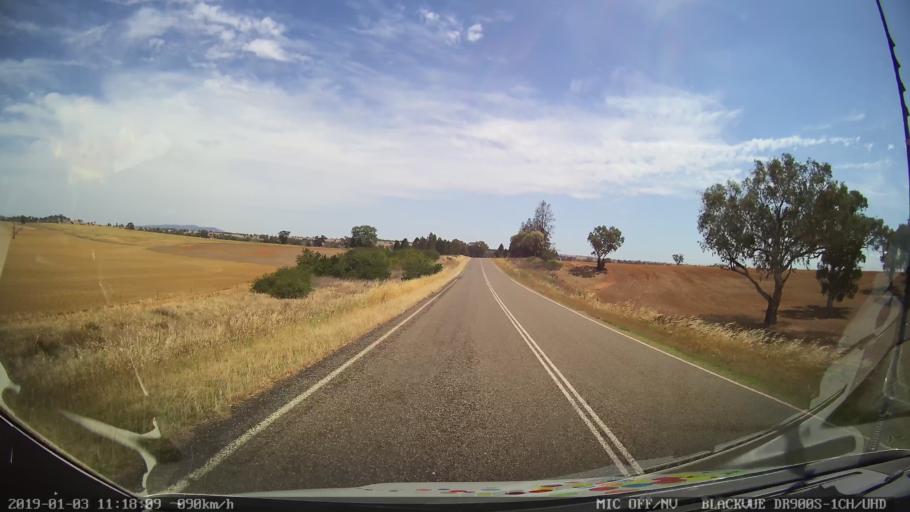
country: AU
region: New South Wales
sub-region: Young
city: Young
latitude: -34.1298
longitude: 148.2639
